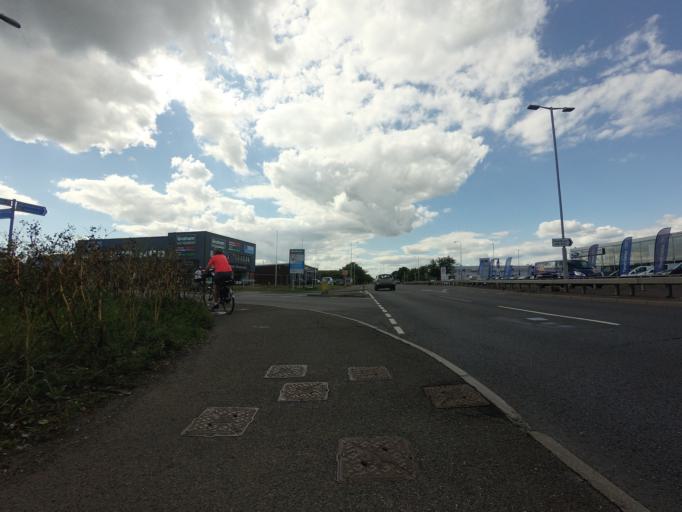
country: GB
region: England
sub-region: East Sussex
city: Eastbourne
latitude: 50.7884
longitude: 0.3015
